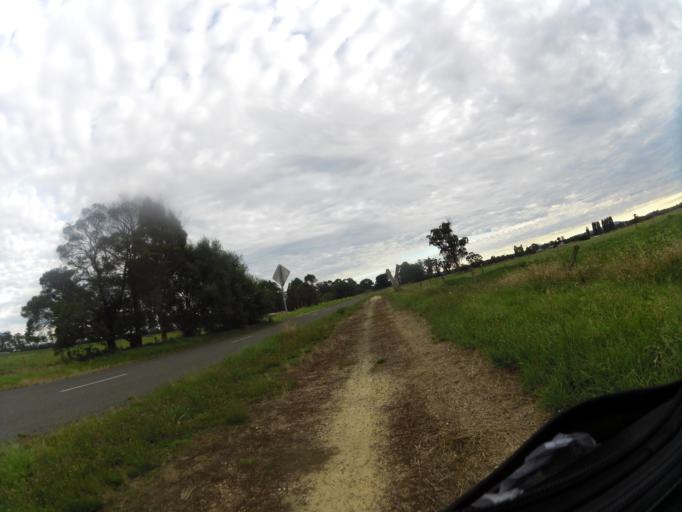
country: AU
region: Victoria
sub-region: East Gippsland
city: Lakes Entrance
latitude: -37.7256
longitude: 148.4404
